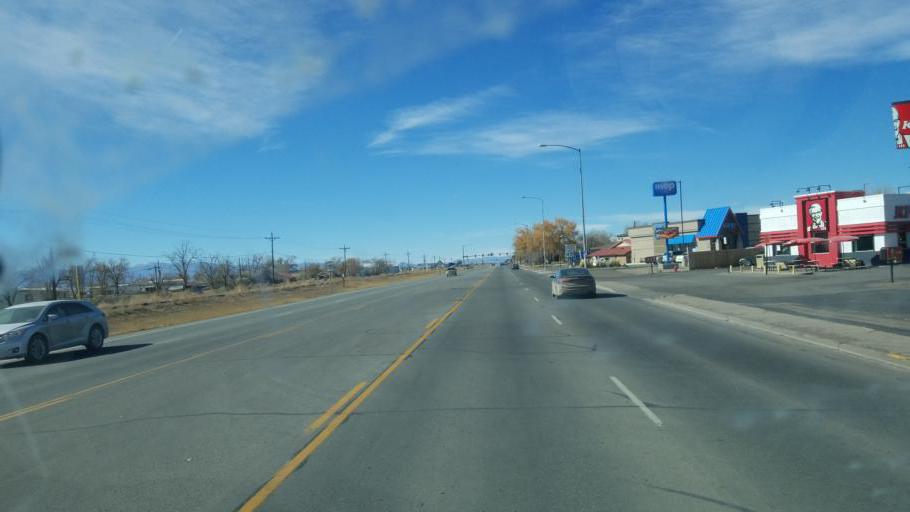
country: US
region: Colorado
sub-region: Alamosa County
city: Alamosa
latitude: 37.4713
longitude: -105.8855
